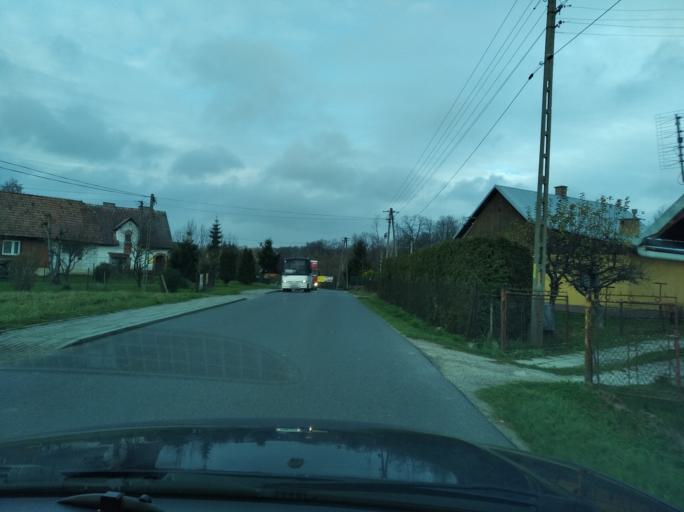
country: PL
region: Subcarpathian Voivodeship
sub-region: Powiat krosnienski
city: Kroscienko Wyzne
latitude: 49.6755
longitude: 21.8209
